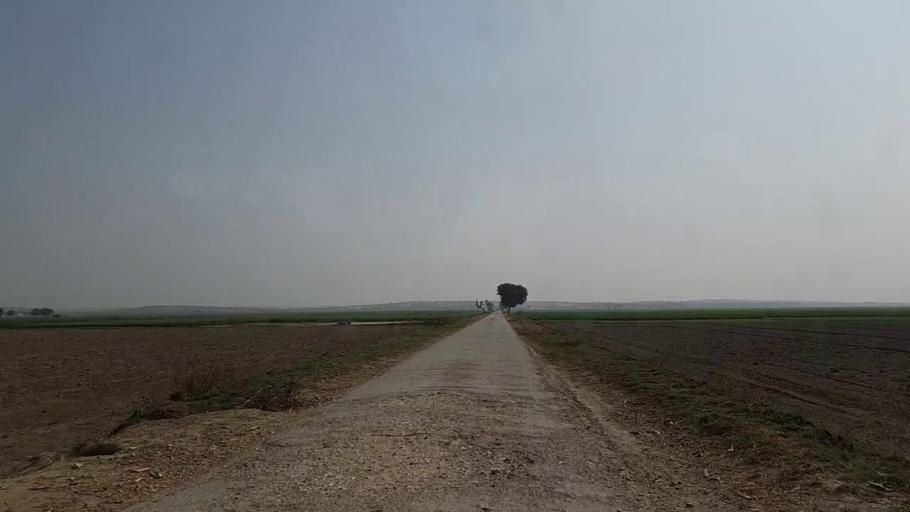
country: PK
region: Sindh
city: Naukot
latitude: 24.7600
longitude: 69.3473
